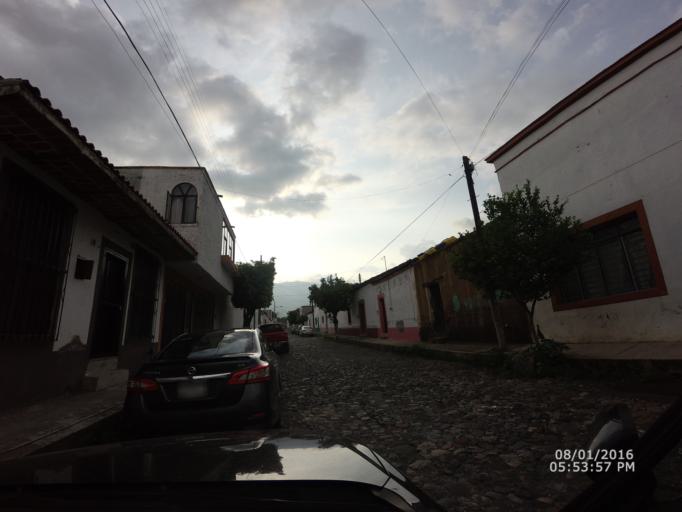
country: MX
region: Nayarit
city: Jala
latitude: 21.1049
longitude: -104.4401
